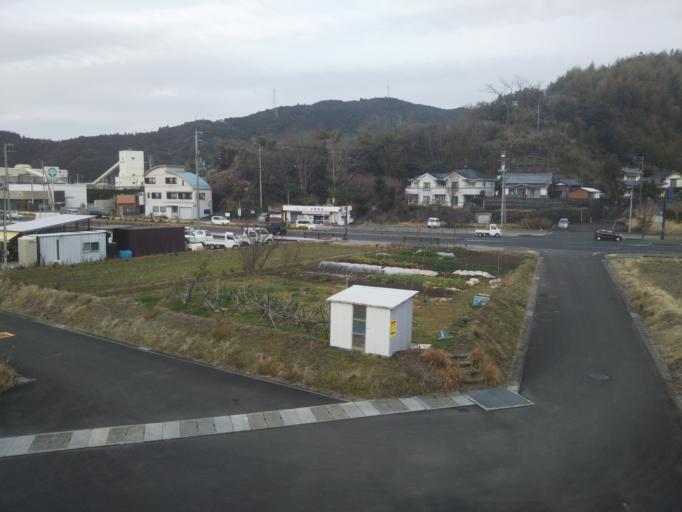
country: JP
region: Kochi
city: Nakamura
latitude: 32.9850
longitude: 132.9613
